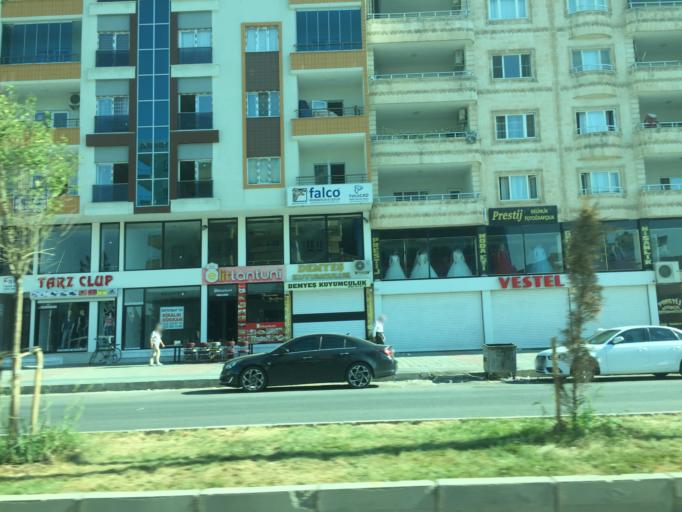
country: TR
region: Mardin
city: Midyat
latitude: 37.4158
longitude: 41.3699
